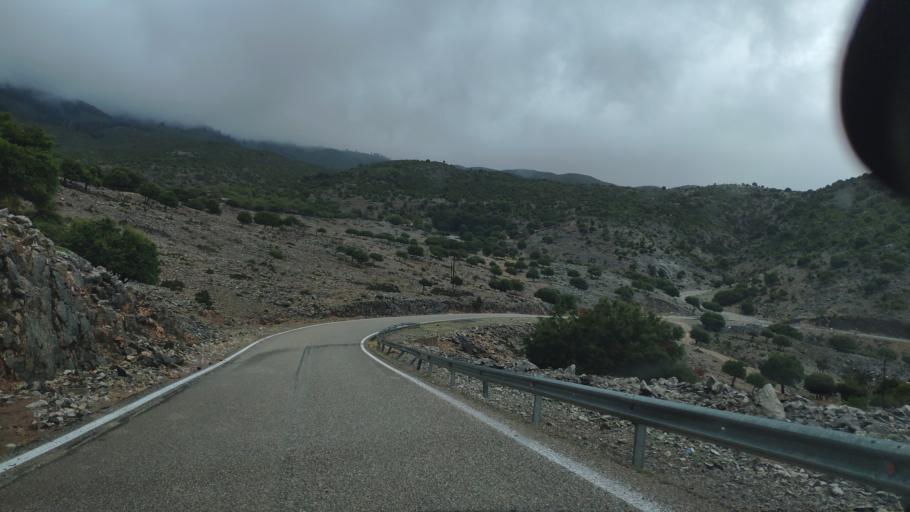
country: GR
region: Central Greece
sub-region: Nomos Evrytanias
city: Kerasochori
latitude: 39.0772
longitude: 21.3992
